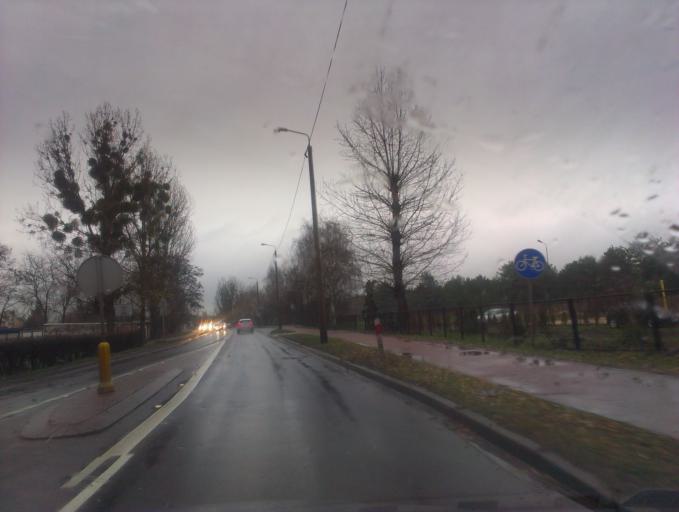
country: PL
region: Greater Poland Voivodeship
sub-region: Powiat obornicki
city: Oborniki
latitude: 52.6500
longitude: 16.8201
